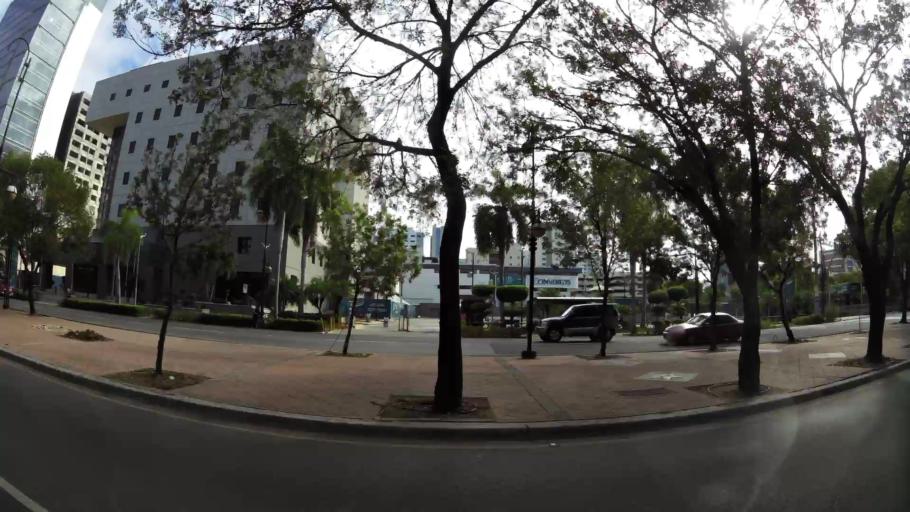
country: DO
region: Nacional
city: La Julia
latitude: 18.4674
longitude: -69.9388
